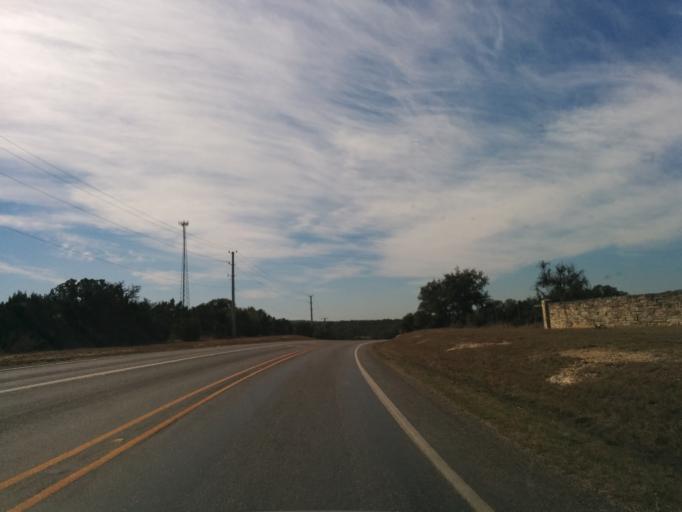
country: US
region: Texas
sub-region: Bexar County
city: Fair Oaks Ranch
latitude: 29.8695
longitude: -98.5592
